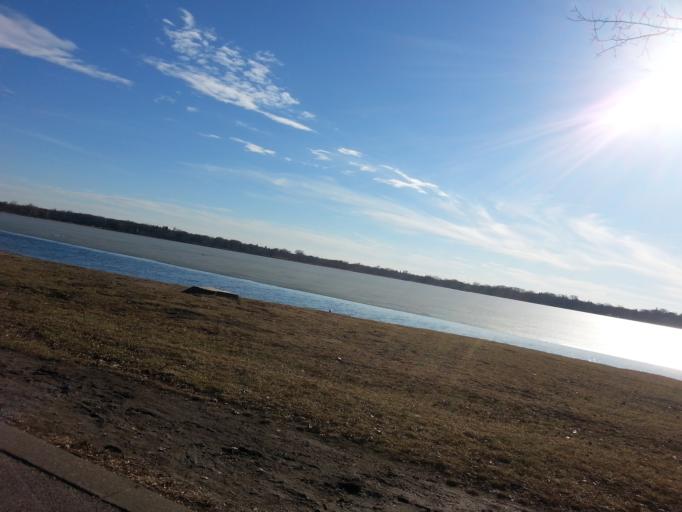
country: US
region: Minnesota
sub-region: Hennepin County
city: Saint Louis Park
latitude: 44.9451
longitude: -93.3051
